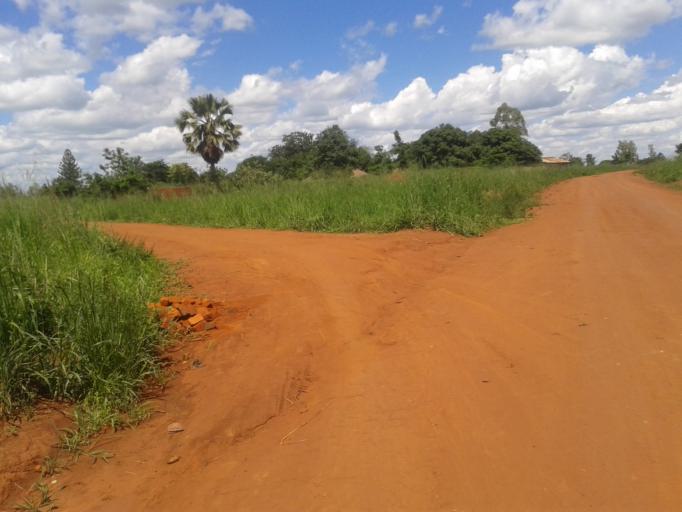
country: UG
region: Northern Region
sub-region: Gulu District
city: Gulu
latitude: 2.7589
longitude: 32.3240
